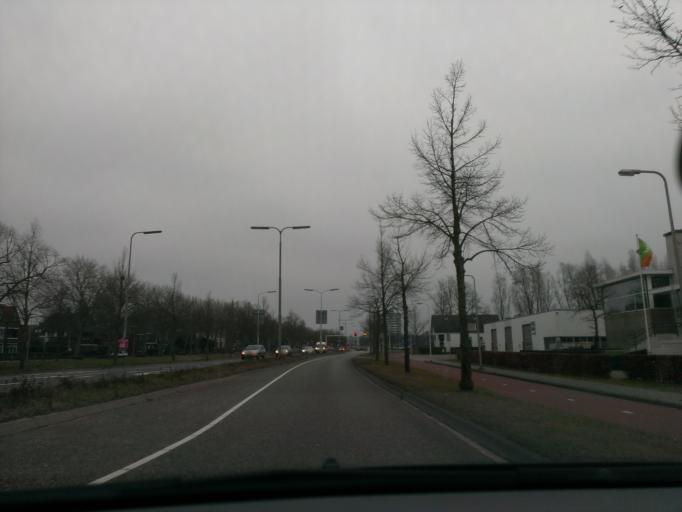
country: NL
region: Overijssel
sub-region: Gemeente Zwolle
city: Zwolle
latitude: 52.5045
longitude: 6.0744
